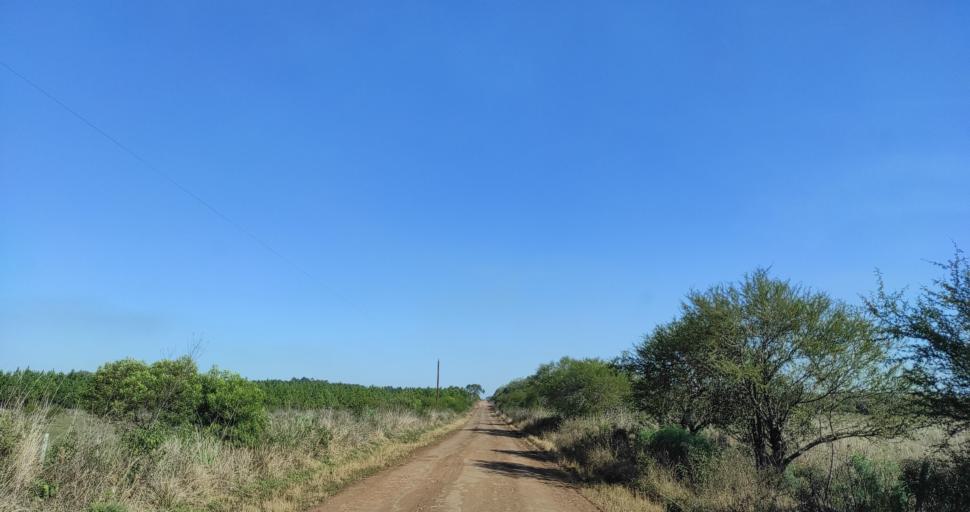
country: AR
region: Misiones
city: Cerro Cora
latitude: -27.6447
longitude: -55.6569
